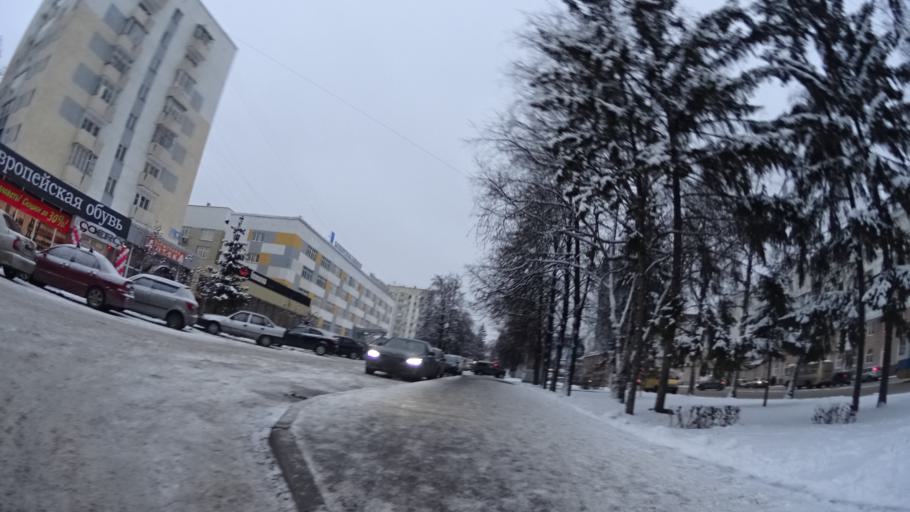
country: RU
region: Bashkortostan
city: Ufa
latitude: 54.7351
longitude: 55.9544
